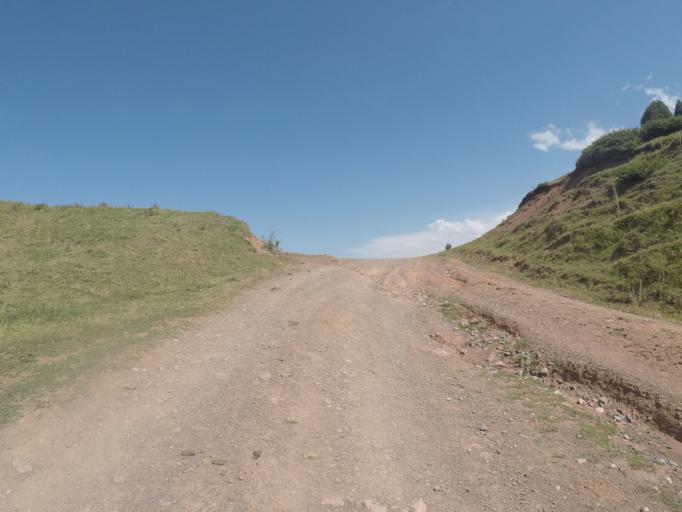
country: KG
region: Chuy
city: Bishkek
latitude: 42.6467
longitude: 74.5610
